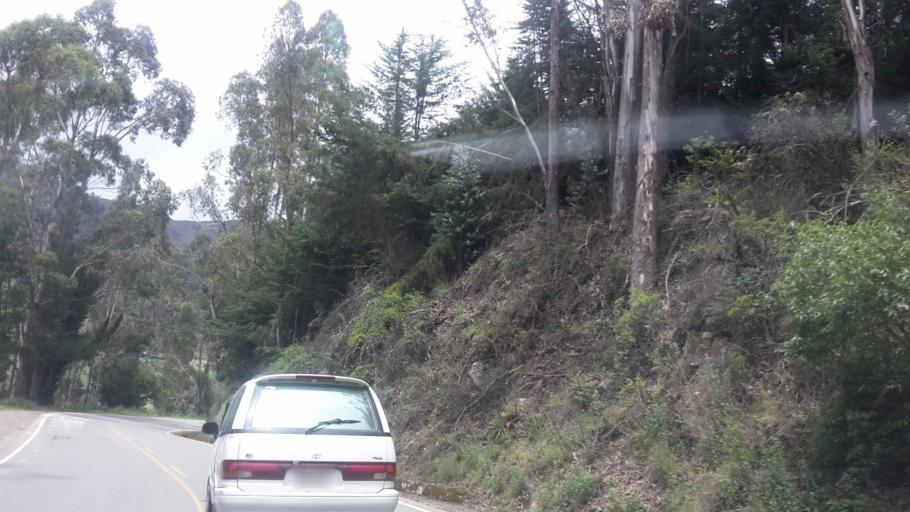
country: BO
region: Cochabamba
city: Totora
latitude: -17.5040
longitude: -65.4139
